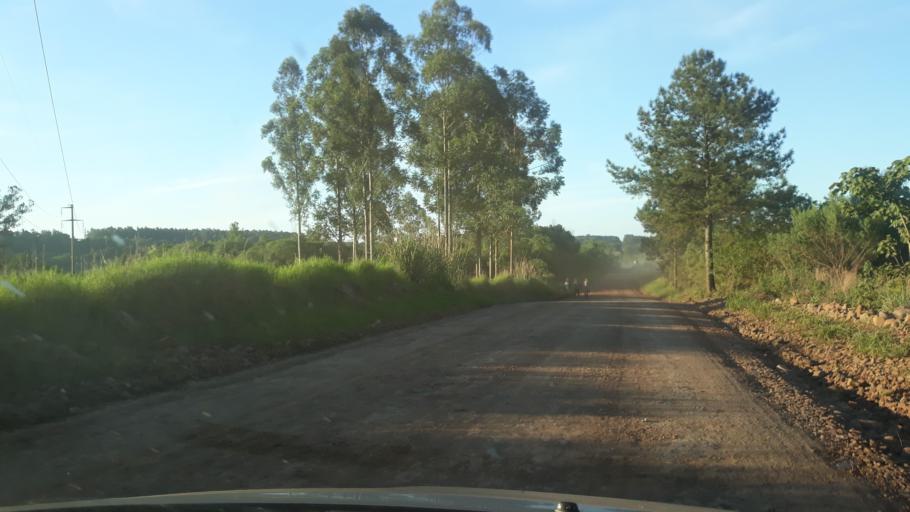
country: AR
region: Misiones
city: Ruiz de Montoya
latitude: -27.0513
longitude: -55.0042
